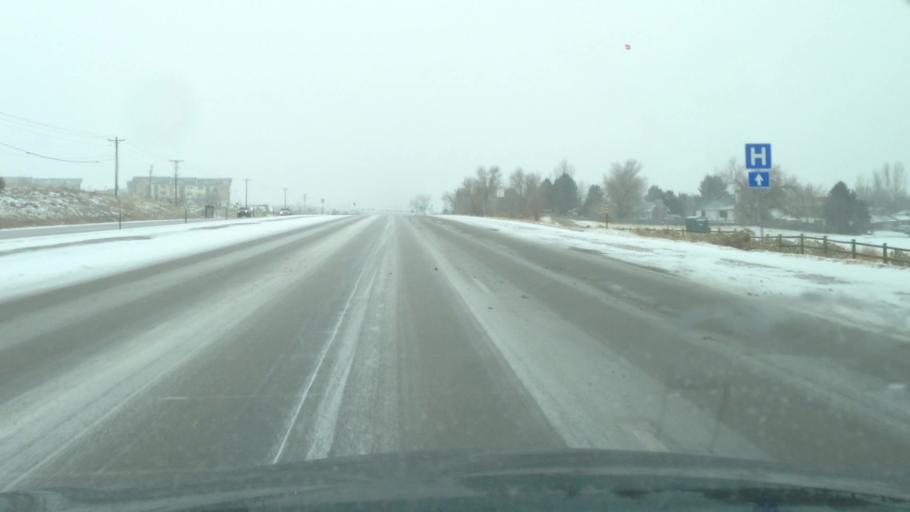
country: US
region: Colorado
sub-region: Douglas County
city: Stonegate
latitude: 39.5640
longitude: -104.7839
